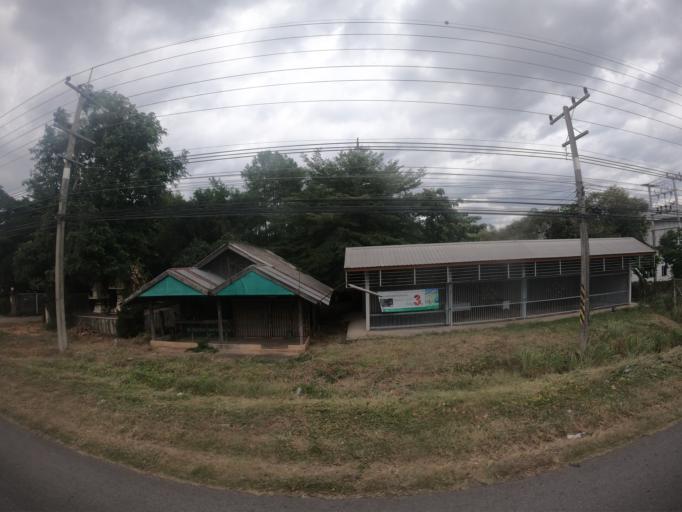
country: TH
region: Nakhon Ratchasima
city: Nakhon Ratchasima
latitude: 14.8903
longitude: 102.1670
